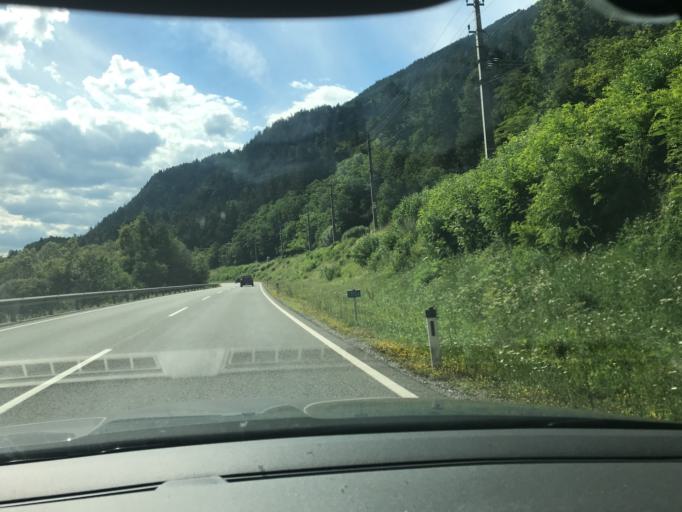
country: AT
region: Tyrol
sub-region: Politischer Bezirk Lienz
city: Leisach
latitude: 46.7938
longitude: 12.7266
